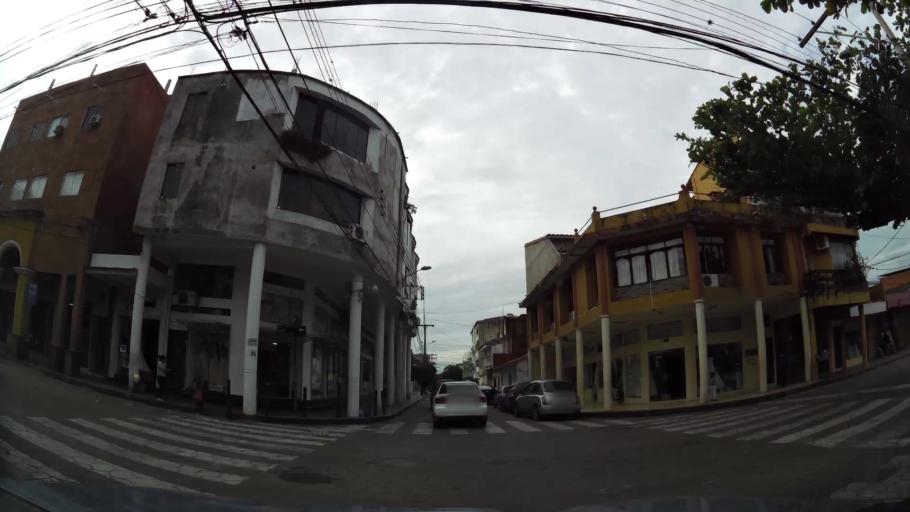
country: BO
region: Santa Cruz
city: Santa Cruz de la Sierra
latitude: -17.7843
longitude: -63.1747
